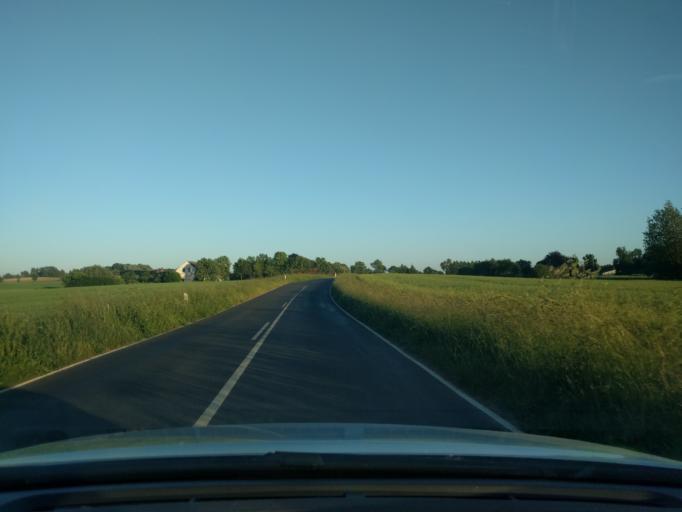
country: DK
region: South Denmark
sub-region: Kerteminde Kommune
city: Kerteminde
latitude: 55.5568
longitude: 10.6529
